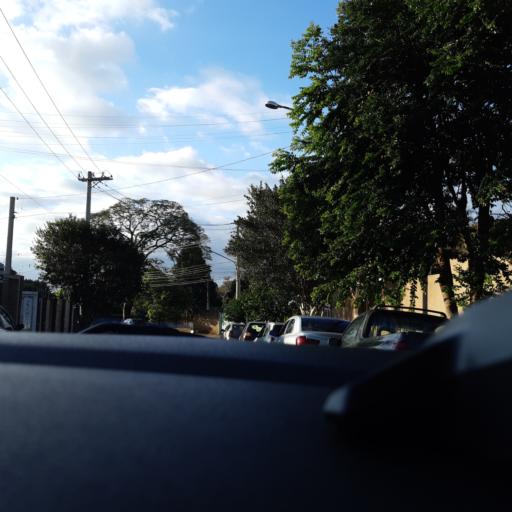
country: BR
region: Sao Paulo
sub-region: Ourinhos
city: Ourinhos
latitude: -22.9834
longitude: -49.8603
